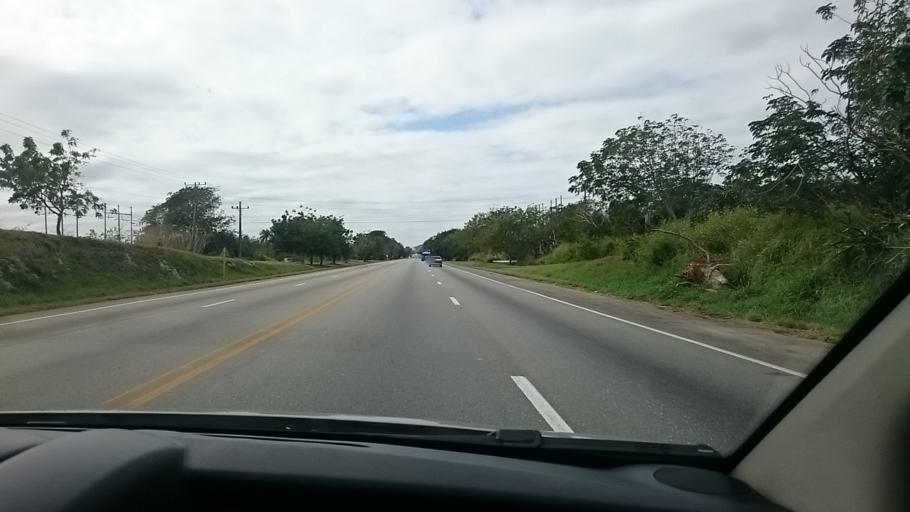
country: CU
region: La Habana
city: Alamar
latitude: 23.1619
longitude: -82.2637
